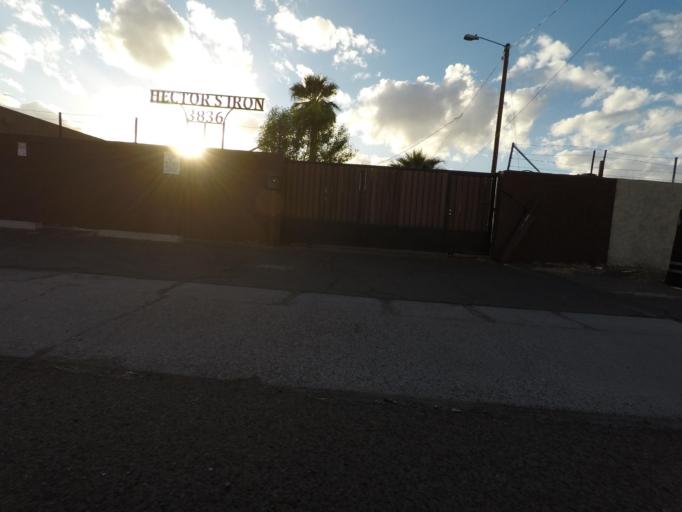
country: US
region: Arizona
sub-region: Maricopa County
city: Glendale
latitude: 33.4929
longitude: -112.1430
